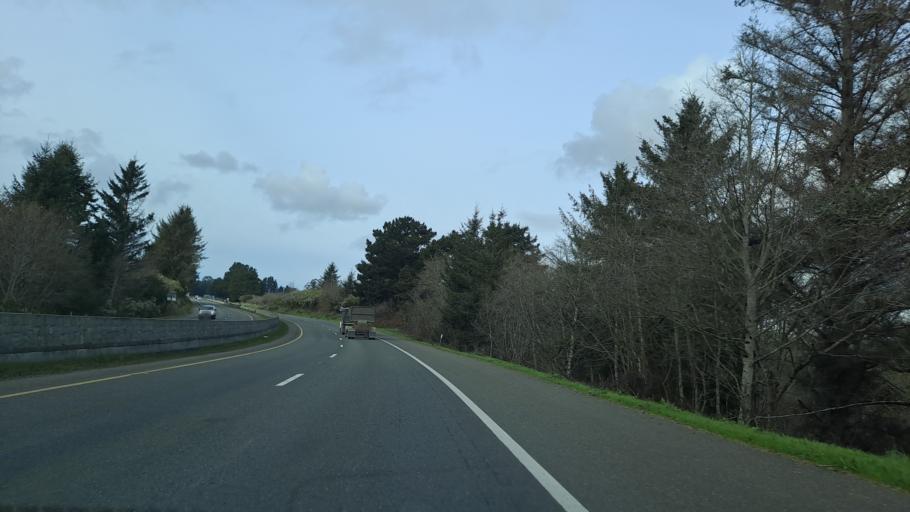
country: US
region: California
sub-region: Humboldt County
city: Fortuna
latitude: 40.6450
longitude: -124.2083
